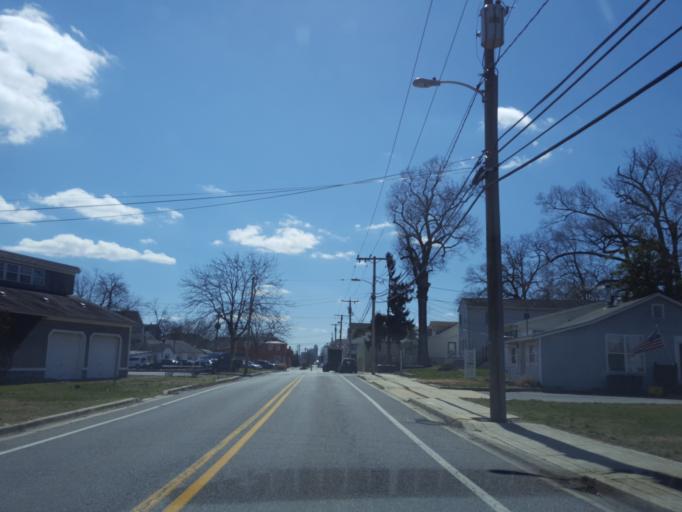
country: US
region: Maryland
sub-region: Calvert County
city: North Beach
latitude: 38.7099
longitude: -76.5310
